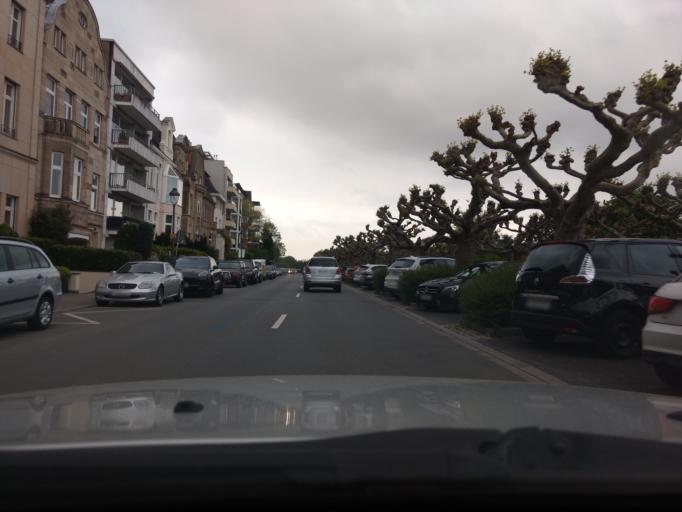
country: DE
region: North Rhine-Westphalia
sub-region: Regierungsbezirk Dusseldorf
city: Dusseldorf
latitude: 51.2352
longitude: 6.7614
